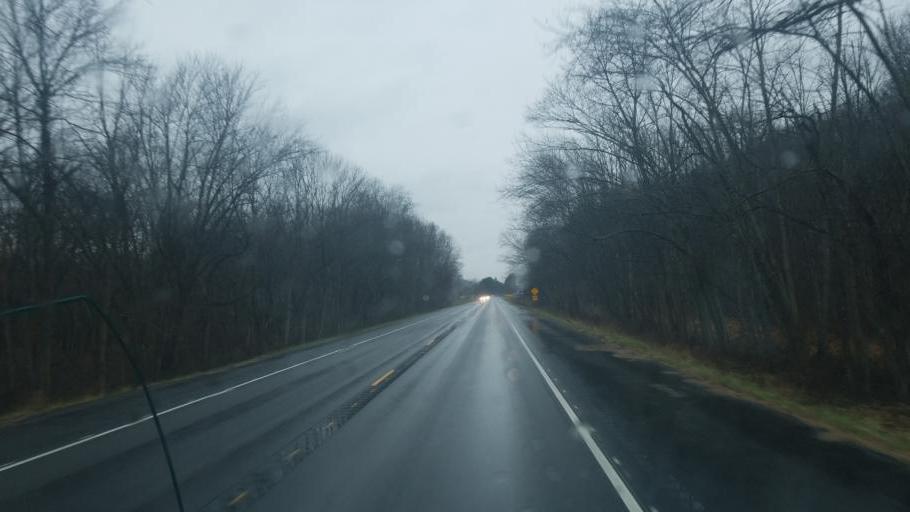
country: US
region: Indiana
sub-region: Brown County
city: Nashville
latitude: 39.1968
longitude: -86.2112
